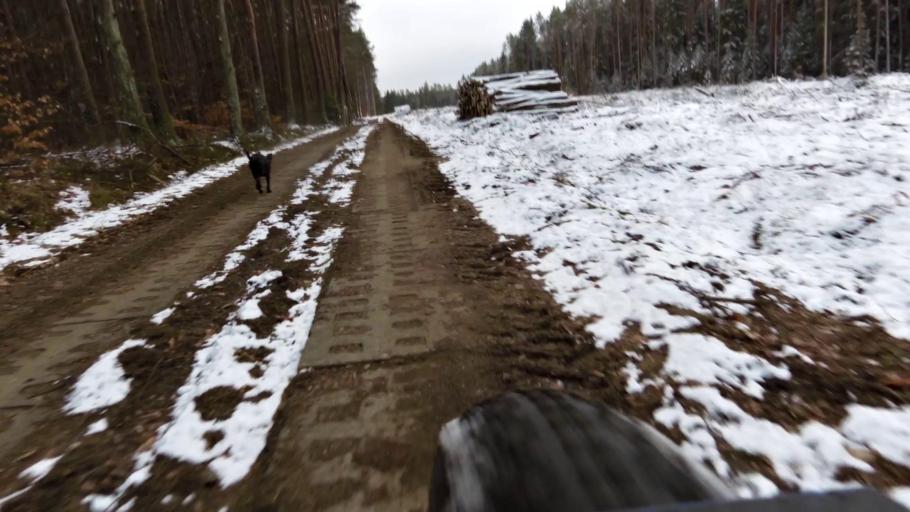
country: PL
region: West Pomeranian Voivodeship
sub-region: Powiat walecki
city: Miroslawiec
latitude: 53.3755
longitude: 16.1475
